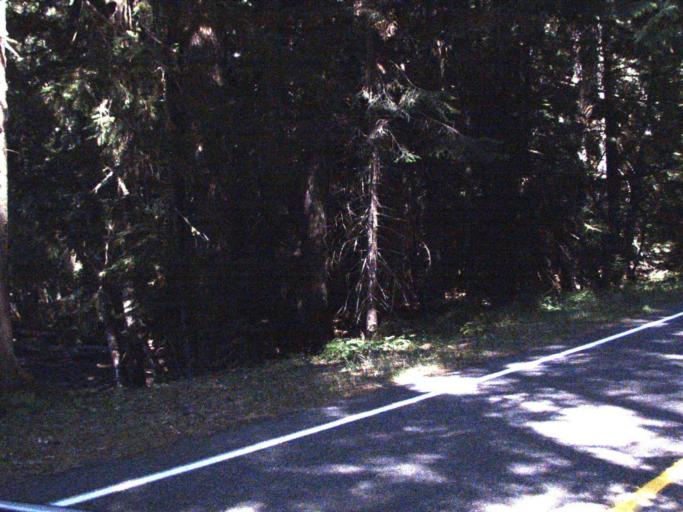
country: US
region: Washington
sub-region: King County
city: Enumclaw
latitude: 46.9592
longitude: -121.5256
